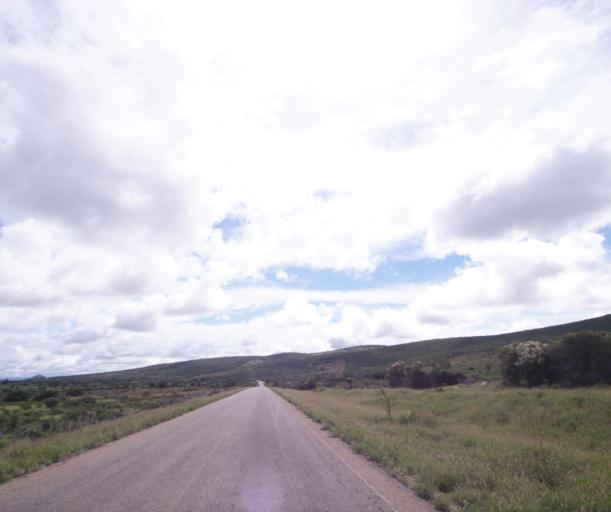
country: BR
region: Bahia
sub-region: Brumado
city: Brumado
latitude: -14.1984
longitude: -41.5934
